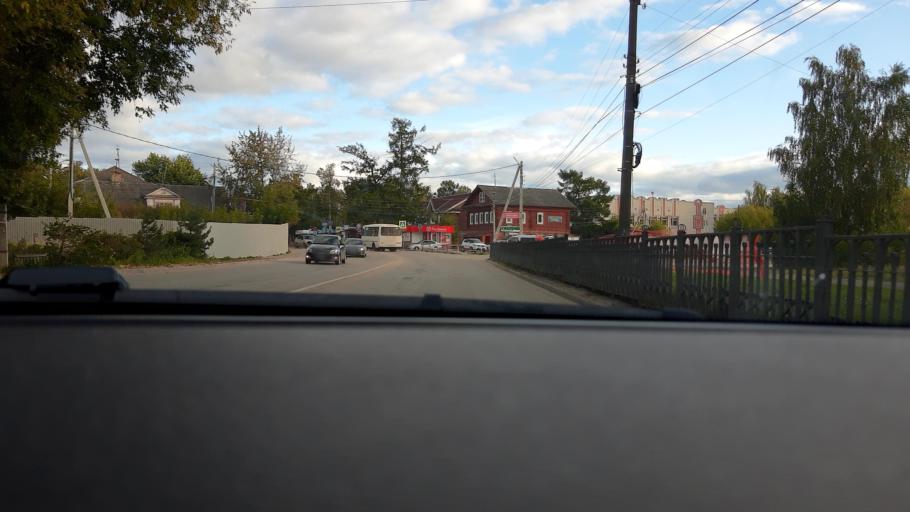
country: RU
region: Nizjnij Novgorod
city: Novaya Balakhna
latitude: 56.4944
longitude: 43.6092
